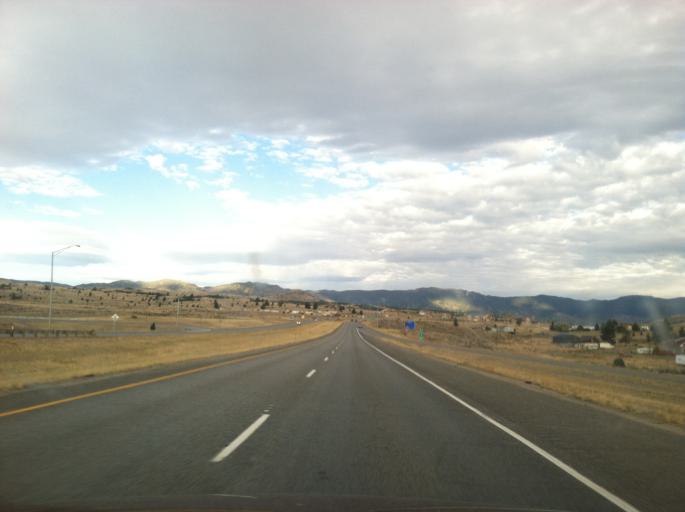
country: US
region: Montana
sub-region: Silver Bow County
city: Butte
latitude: 46.0081
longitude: -112.6377
